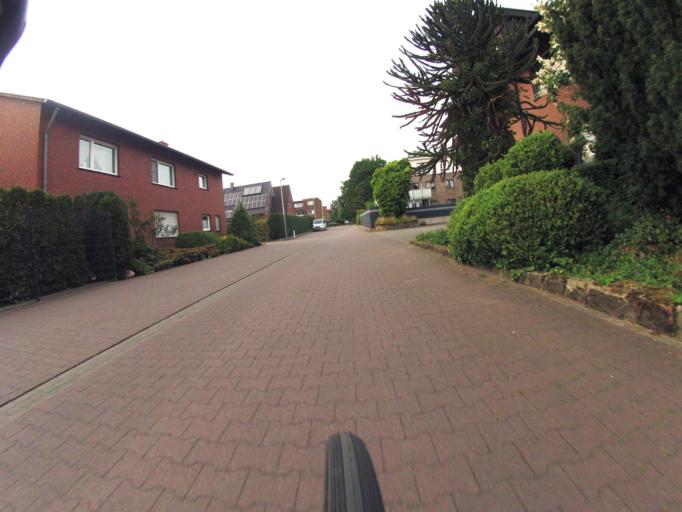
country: DE
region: North Rhine-Westphalia
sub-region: Regierungsbezirk Munster
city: Mettingen
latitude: 52.2652
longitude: 7.7809
